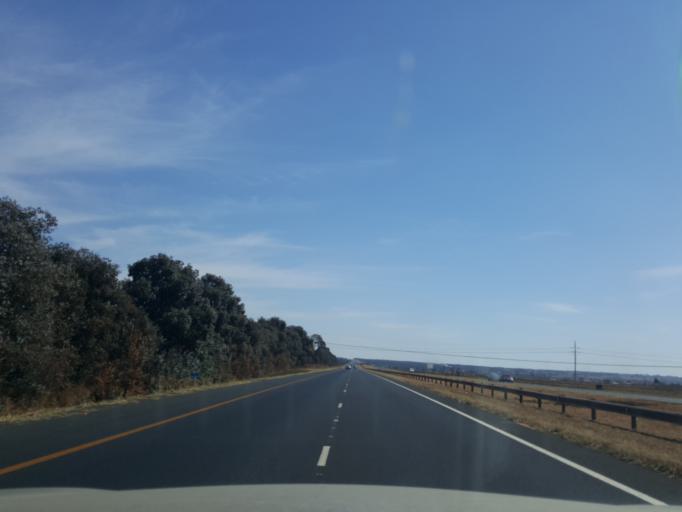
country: ZA
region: Mpumalanga
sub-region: Nkangala District Municipality
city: Witbank
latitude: -25.8725
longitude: 29.1075
